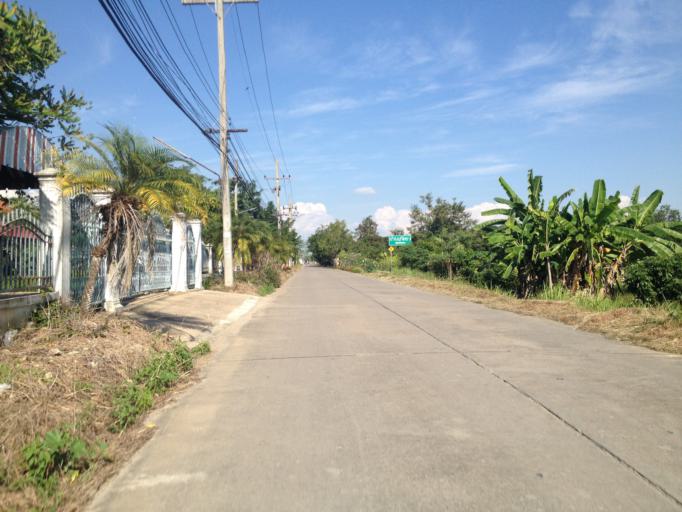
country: TH
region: Chiang Mai
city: Hang Dong
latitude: 18.7298
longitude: 98.9565
